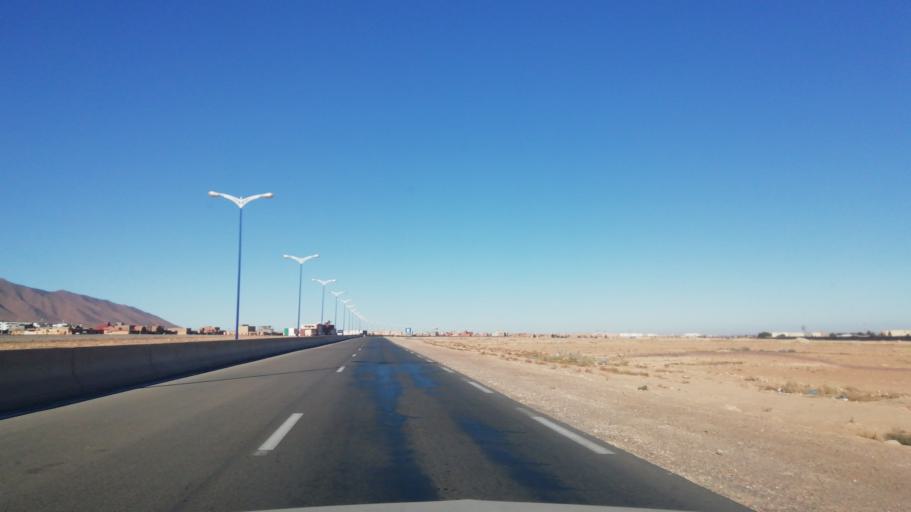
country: DZ
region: Wilaya de Naama
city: Naama
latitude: 33.5248
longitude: -0.2743
